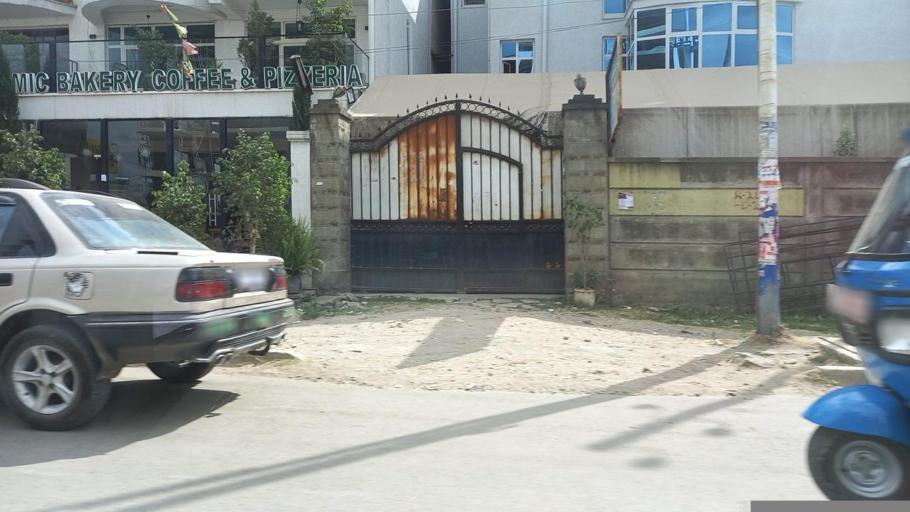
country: ET
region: Adis Abeba
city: Addis Ababa
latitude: 9.0097
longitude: 38.8585
